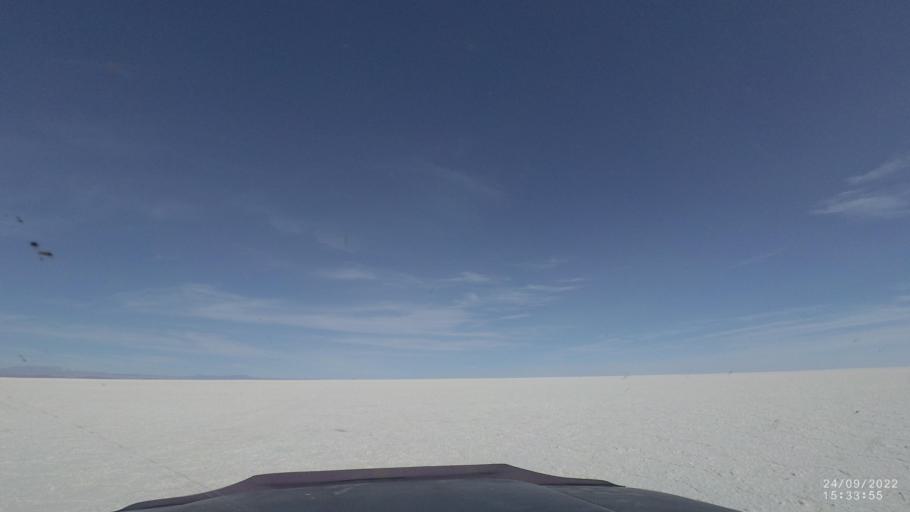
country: BO
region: Potosi
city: Colchani
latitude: -20.1194
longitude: -67.2669
